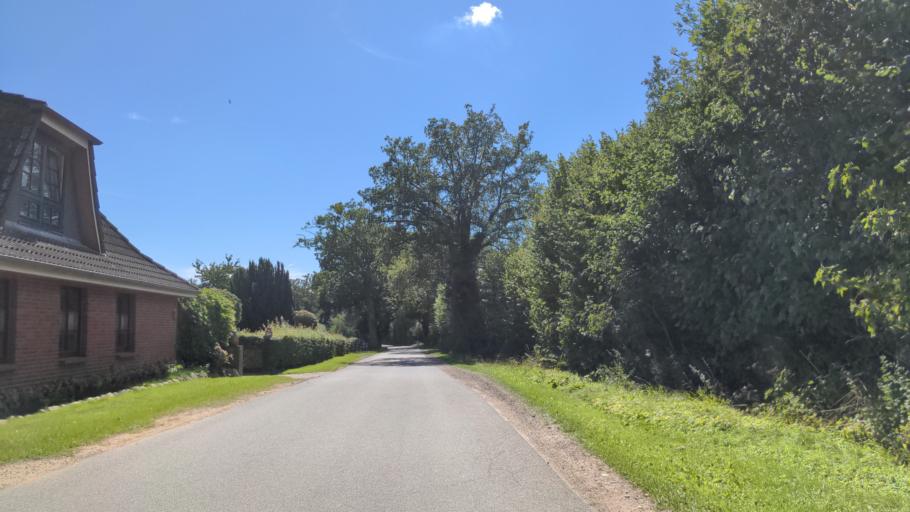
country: DE
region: Schleswig-Holstein
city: Beschendorf
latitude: 54.1990
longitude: 10.8229
